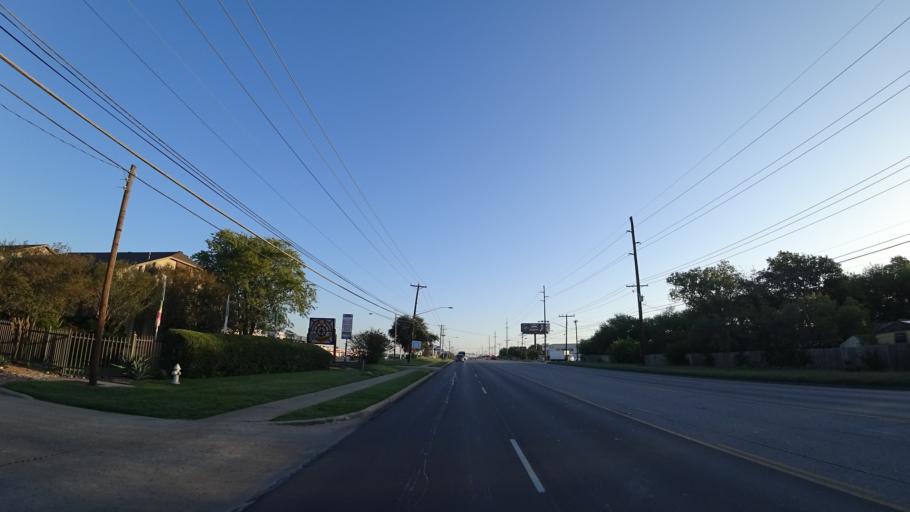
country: US
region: Texas
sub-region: Travis County
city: Wells Branch
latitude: 30.3604
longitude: -97.6986
